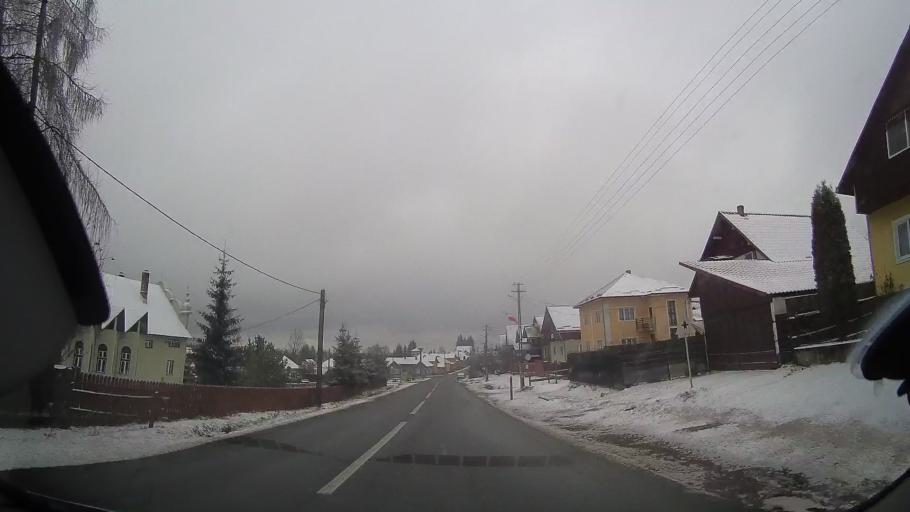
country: RO
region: Cluj
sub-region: Comuna Belis
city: Belis
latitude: 46.6829
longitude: 23.0333
